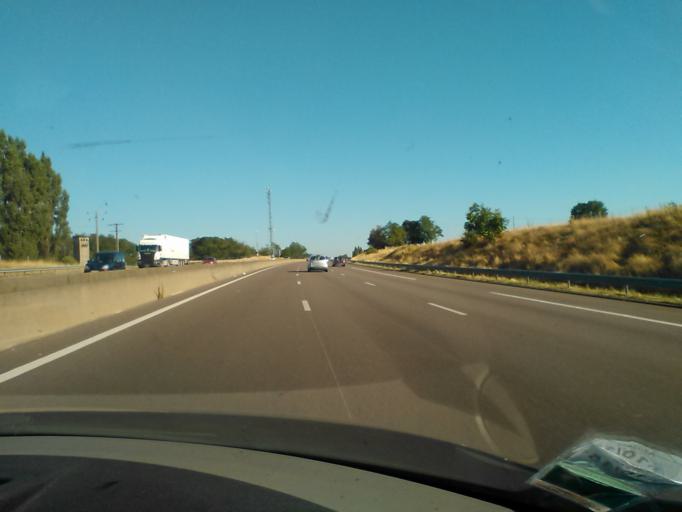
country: FR
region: Bourgogne
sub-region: Departement de Saone-et-Loire
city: Tournus
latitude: 46.5791
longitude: 4.8992
